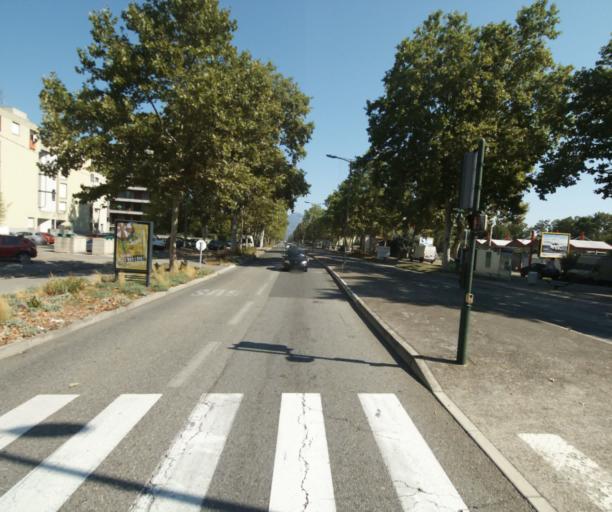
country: FR
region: Rhone-Alpes
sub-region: Departement de l'Isere
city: Le Pont-de-Claix
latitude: 45.1278
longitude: 5.6987
